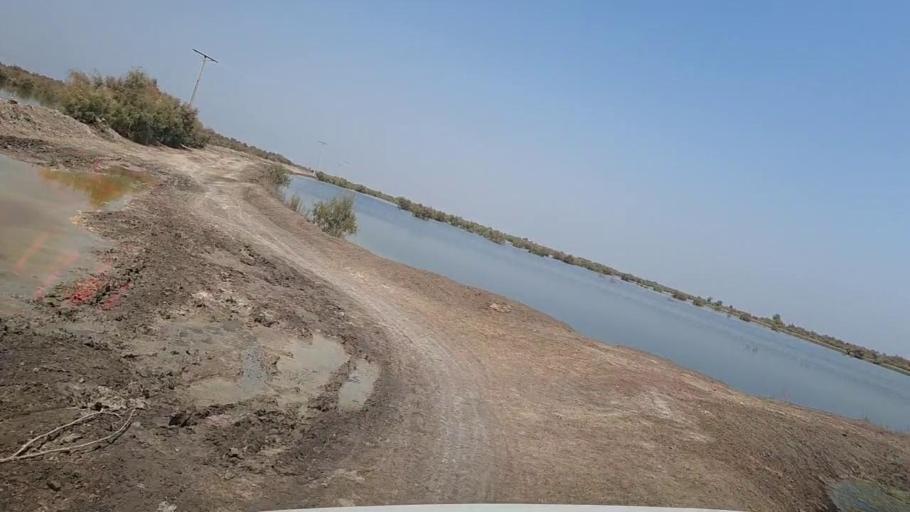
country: PK
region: Sindh
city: Kandhkot
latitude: 28.3455
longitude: 69.3018
